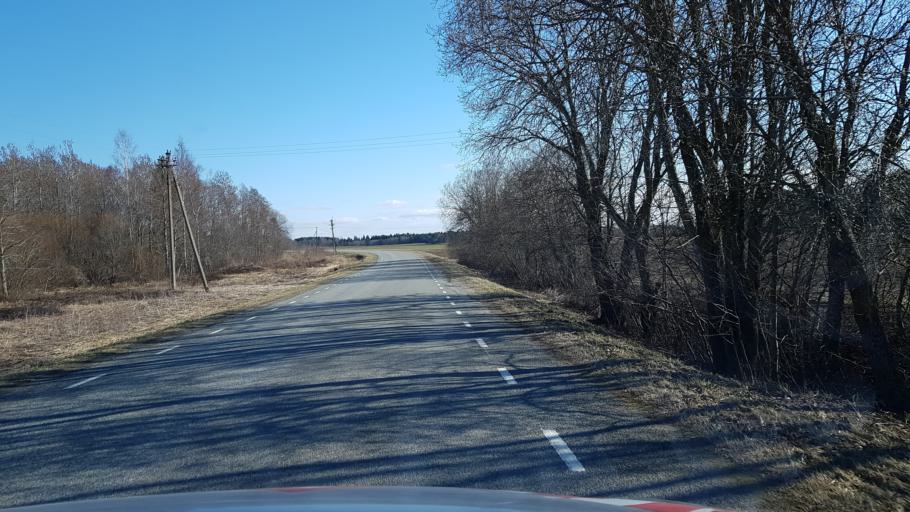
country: EE
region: Laeaene-Virumaa
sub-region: Kadrina vald
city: Kadrina
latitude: 59.3684
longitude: 26.0479
